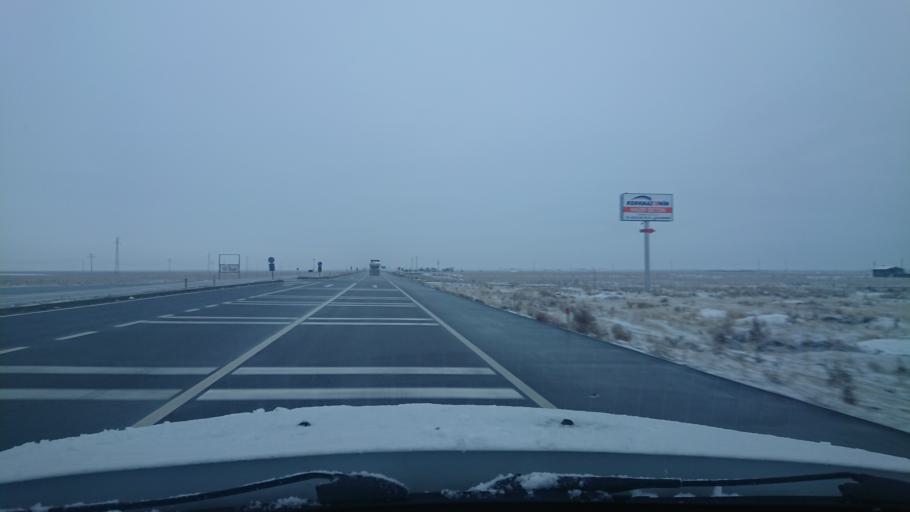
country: TR
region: Aksaray
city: Sultanhani
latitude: 38.2542
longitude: 33.5849
